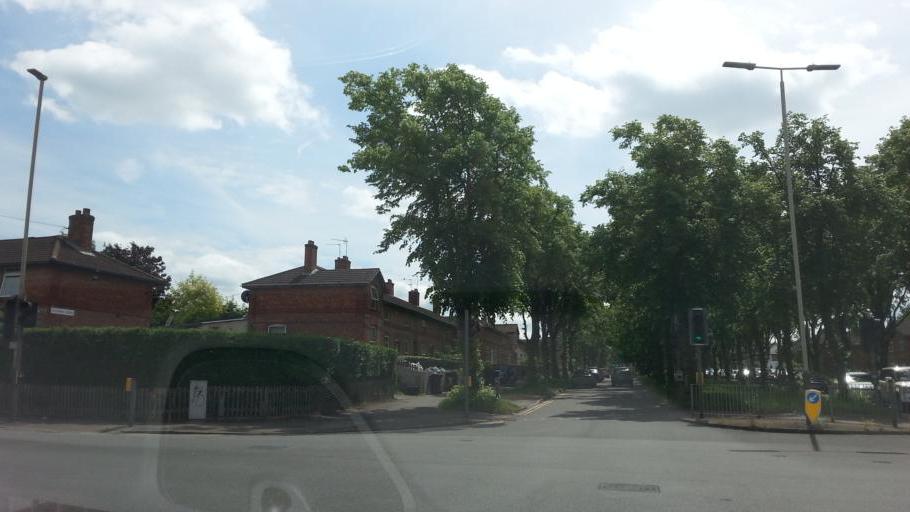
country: GB
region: England
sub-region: Leicestershire
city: Oadby
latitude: 52.6380
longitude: -1.0907
